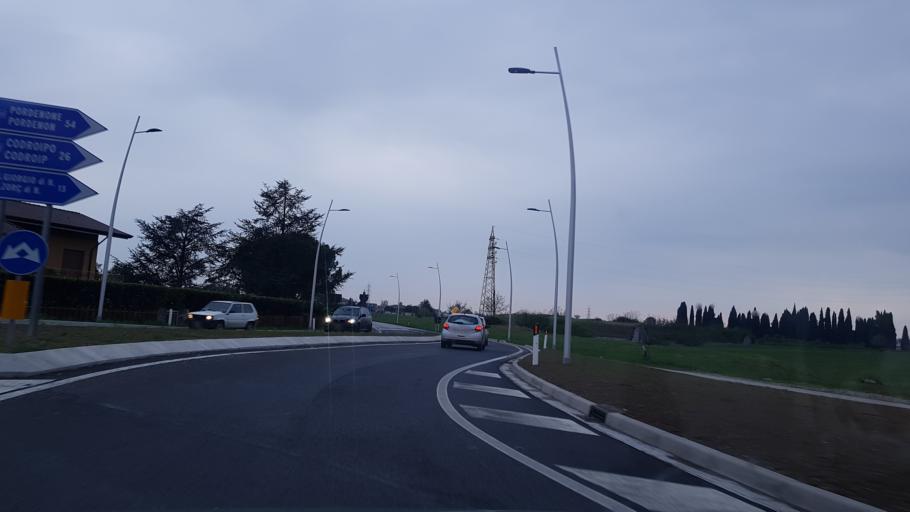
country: IT
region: Friuli Venezia Giulia
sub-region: Provincia di Udine
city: Palmanova
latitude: 45.8991
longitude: 13.3093
